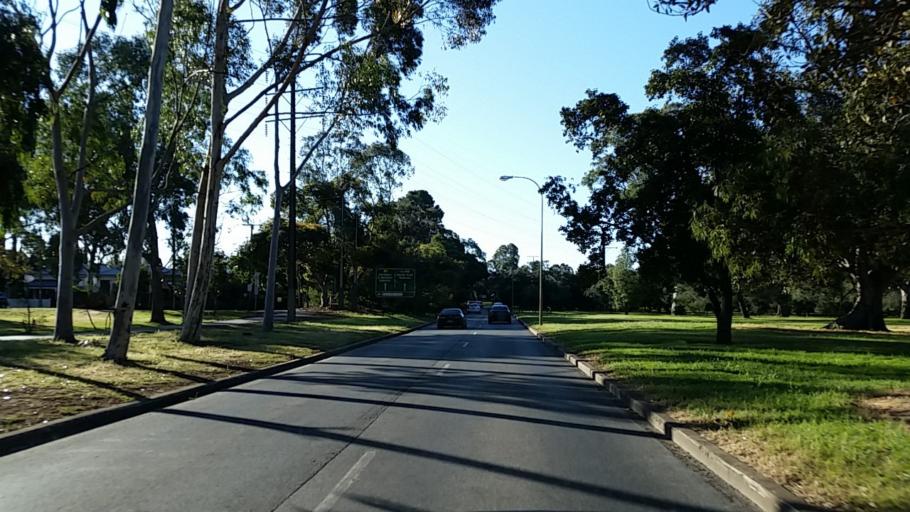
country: AU
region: South Australia
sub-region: Adelaide
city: North Adelaide
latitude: -34.9067
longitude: 138.6124
